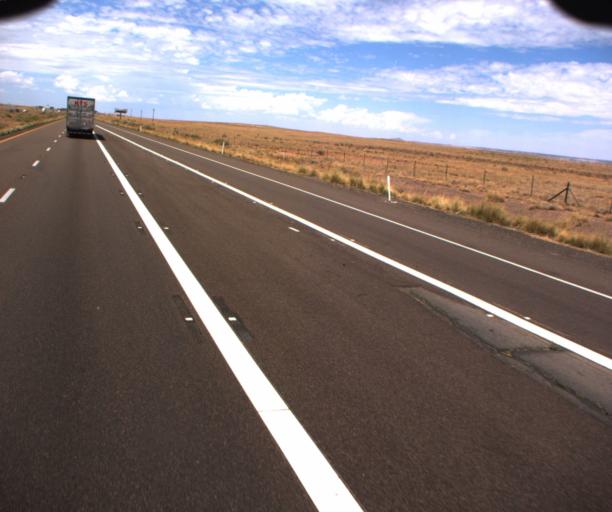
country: US
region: Arizona
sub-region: Navajo County
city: Holbrook
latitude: 34.9797
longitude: -110.0613
